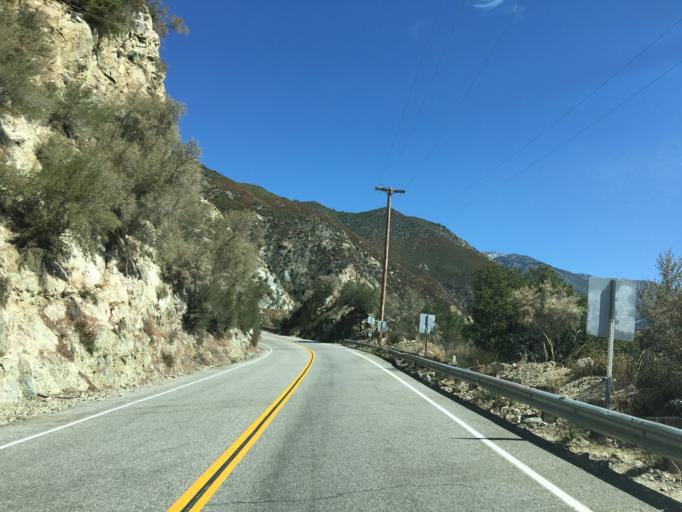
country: US
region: California
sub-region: San Bernardino County
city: San Antonio Heights
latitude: 34.2071
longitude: -117.6758
